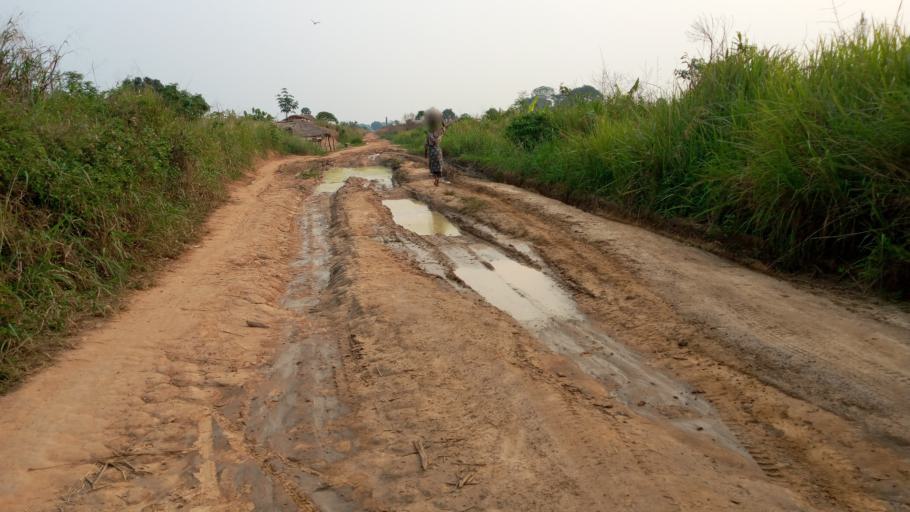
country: CD
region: Bandundu
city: Bandundu
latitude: -3.4215
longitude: 17.6102
